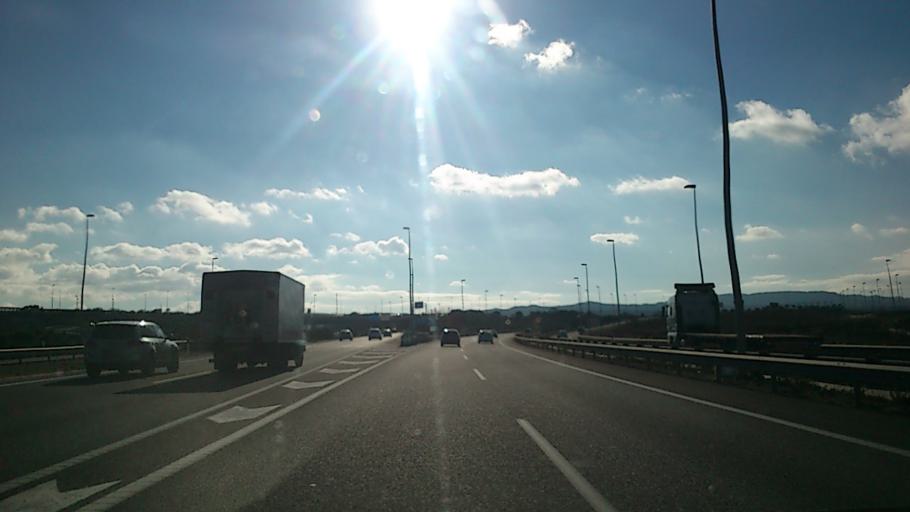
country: ES
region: Aragon
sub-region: Provincia de Zaragoza
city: Montecanal
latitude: 41.6393
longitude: -0.9729
